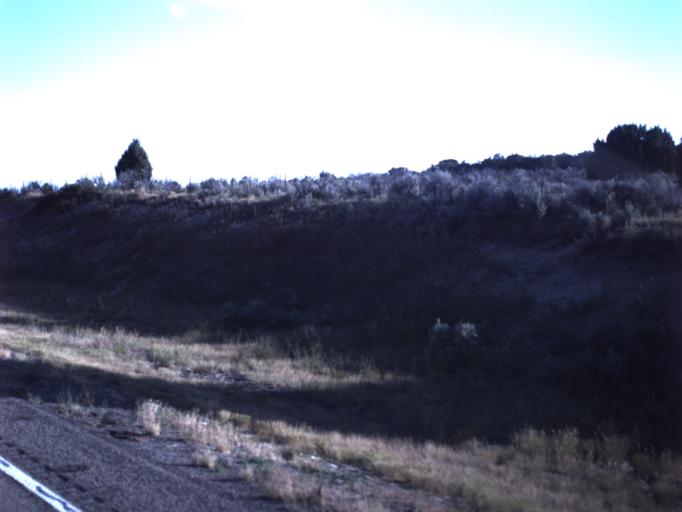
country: US
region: Utah
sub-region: Sanpete County
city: Fairview
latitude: 39.6896
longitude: -111.4599
